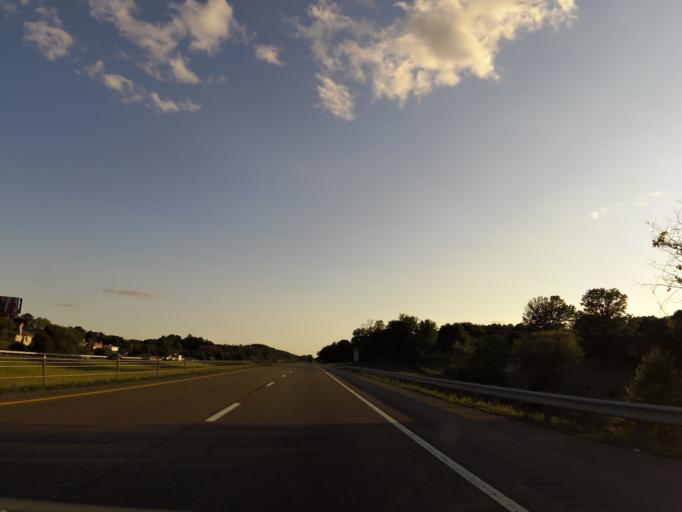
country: US
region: Tennessee
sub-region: Sullivan County
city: Blountville
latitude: 36.5258
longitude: -82.3976
